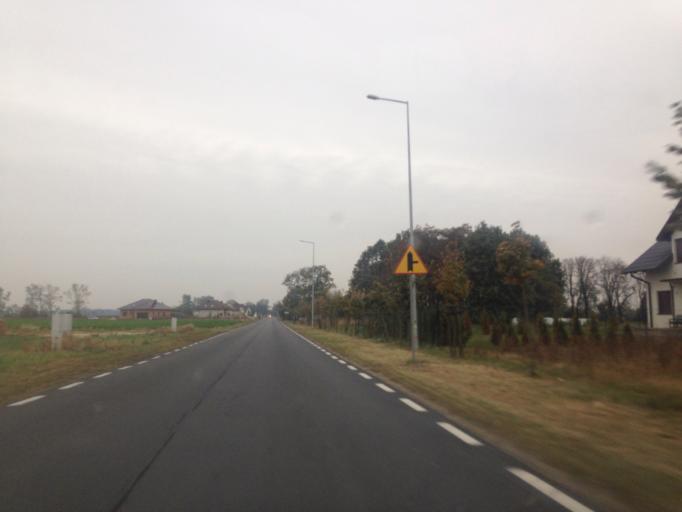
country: PL
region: Greater Poland Voivodeship
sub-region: Powiat poznanski
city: Kleszczewo
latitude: 52.3582
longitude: 17.1259
